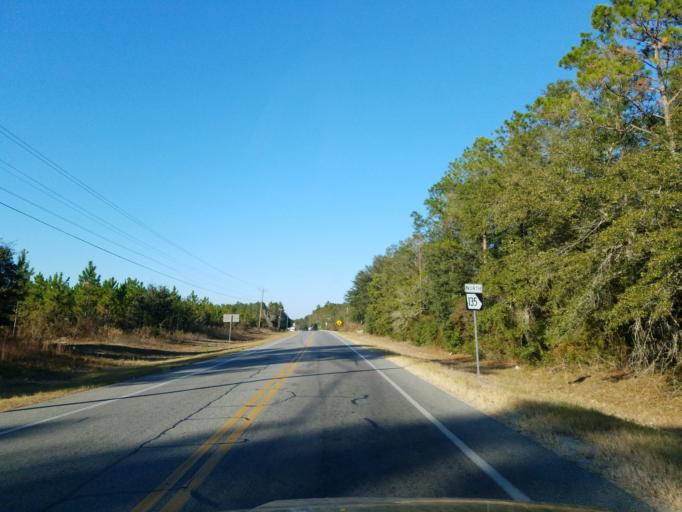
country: US
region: Georgia
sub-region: Echols County
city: Statenville
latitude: 30.7079
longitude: -83.0605
